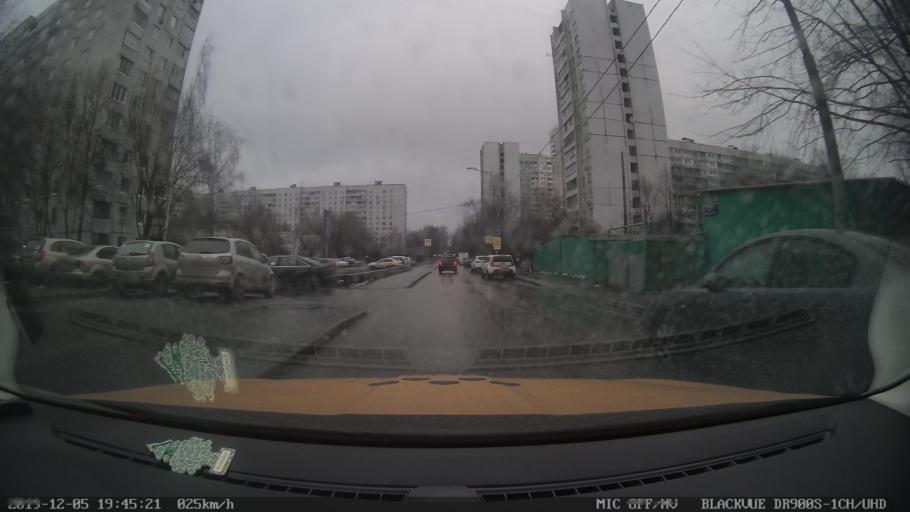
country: RU
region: Moscow
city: Lianozovo
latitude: 55.9031
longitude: 37.5767
